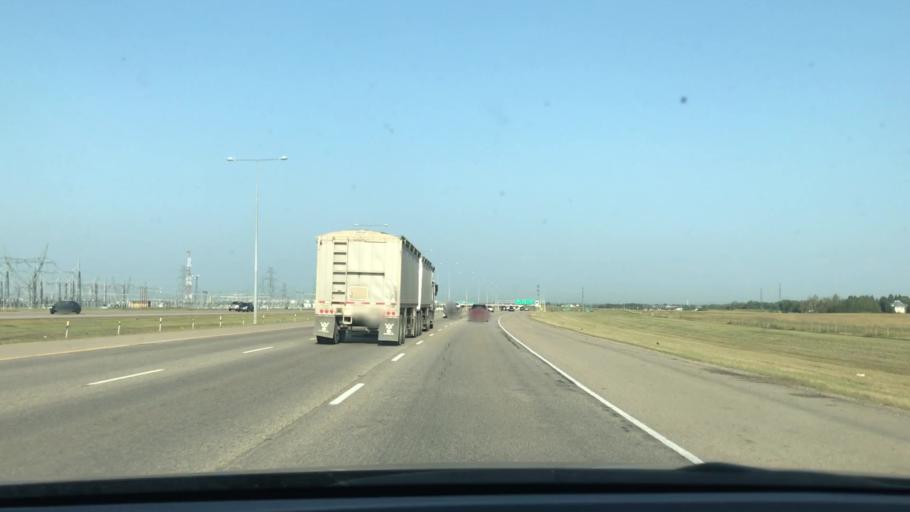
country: CA
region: Alberta
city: Beaumont
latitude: 53.4360
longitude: -113.4460
